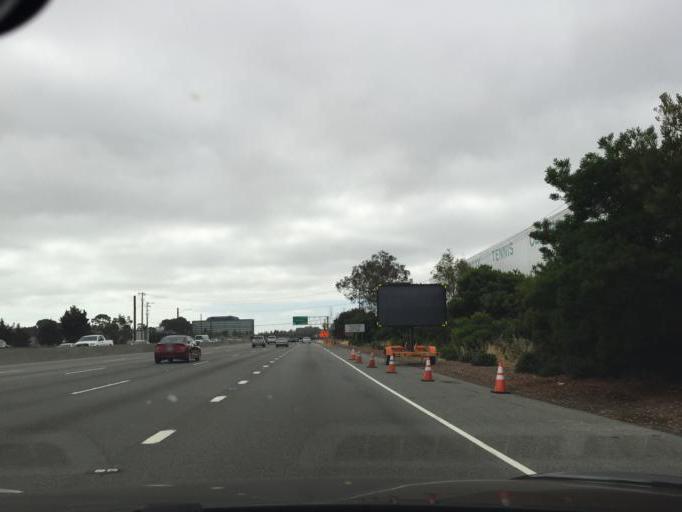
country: US
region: California
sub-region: San Mateo County
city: Burlingame
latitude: 37.5936
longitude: -122.3670
